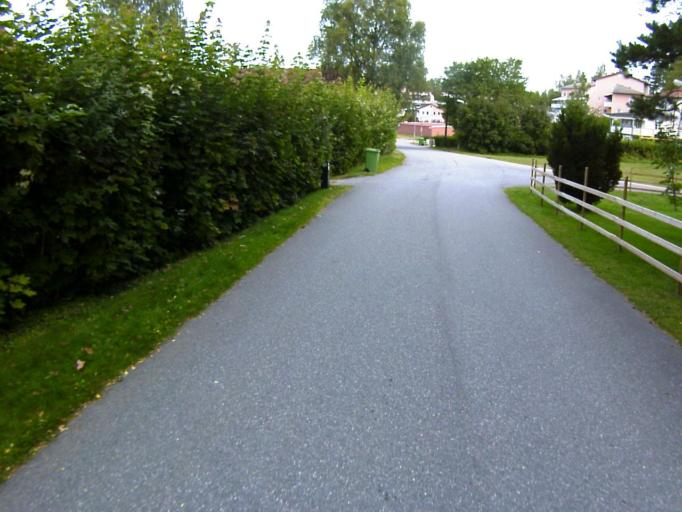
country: SE
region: Soedermanland
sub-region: Eskilstuna Kommun
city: Skogstorp
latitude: 59.2919
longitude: 16.4548
